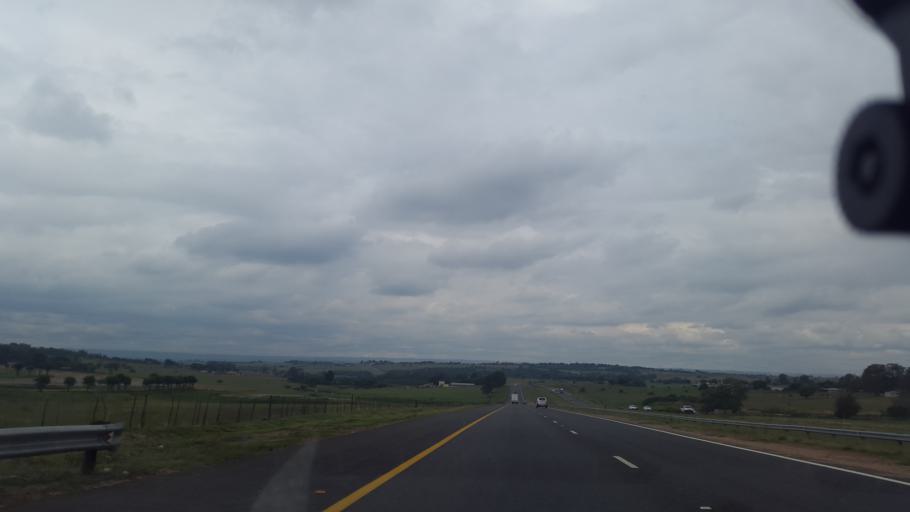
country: ZA
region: Gauteng
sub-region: West Rand District Municipality
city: Muldersdriseloop
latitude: -26.0113
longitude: 27.8830
